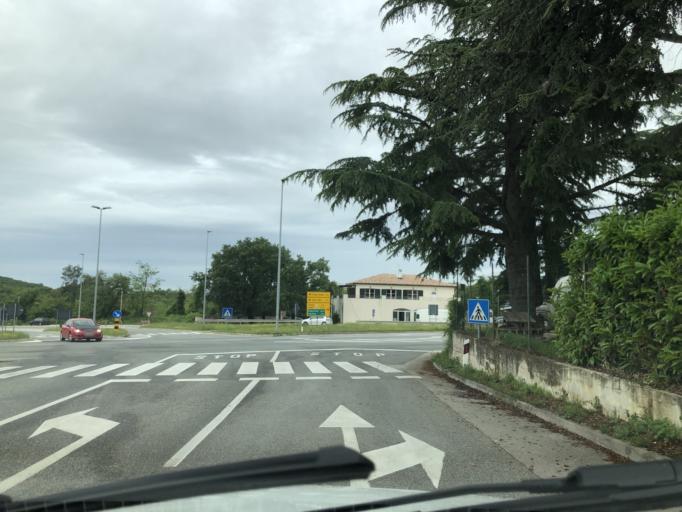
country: HR
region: Istarska
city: Buje
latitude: 45.4506
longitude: 13.6365
